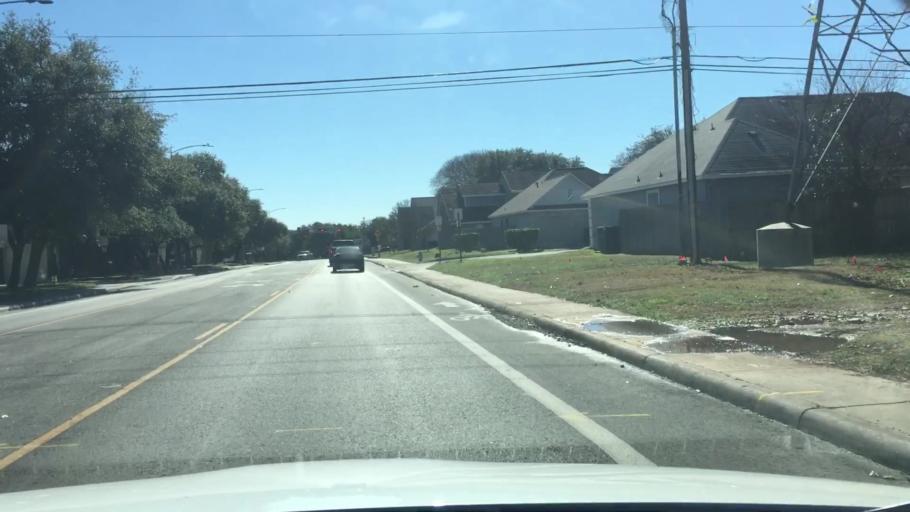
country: US
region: Texas
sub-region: Bexar County
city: Hollywood Park
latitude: 29.5946
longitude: -98.4534
